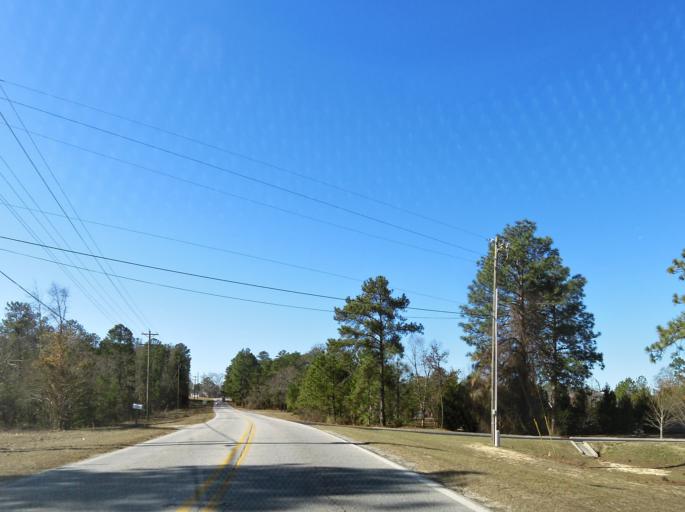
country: US
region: Georgia
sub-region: Bibb County
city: West Point
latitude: 32.7477
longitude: -83.7328
